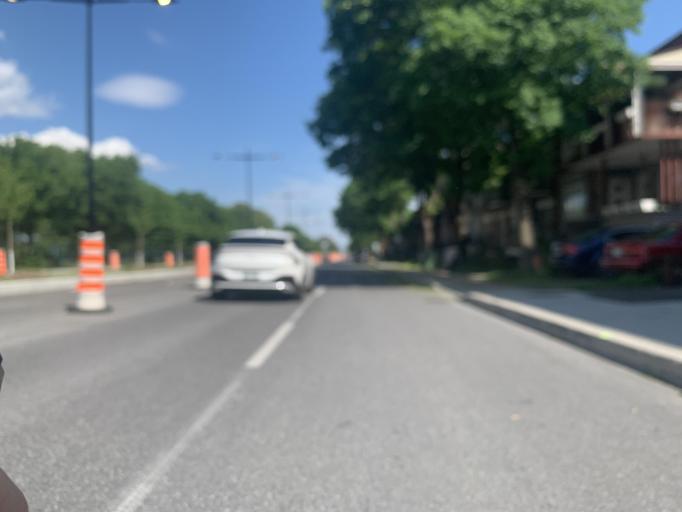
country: CA
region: Quebec
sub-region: Montreal
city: Saint-Leonard
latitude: 45.5597
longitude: -73.5707
